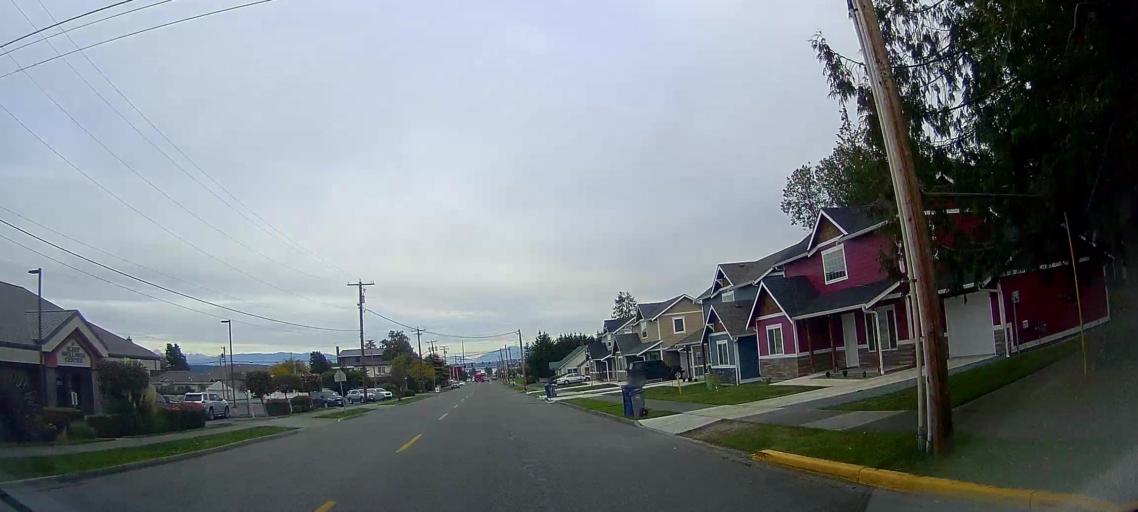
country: US
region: Washington
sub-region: Skagit County
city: Anacortes
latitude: 48.5046
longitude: -122.6158
